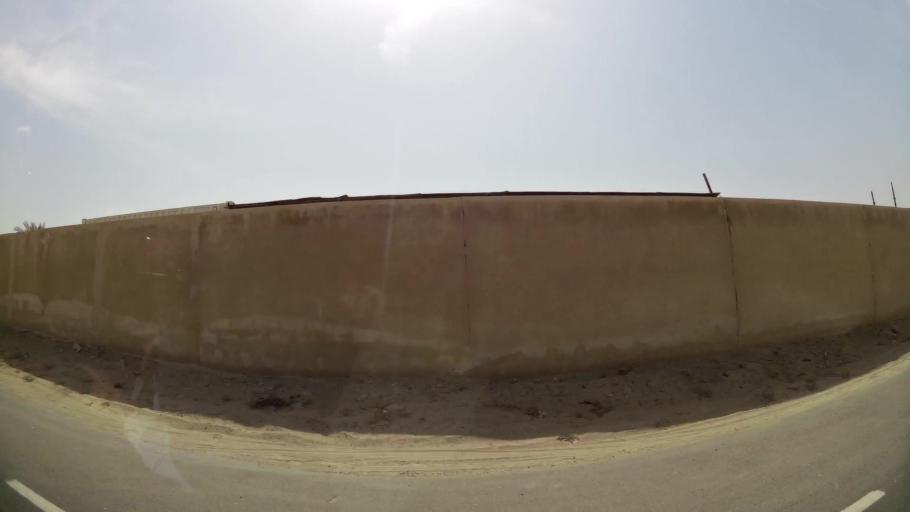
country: AE
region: Ash Shariqah
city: Sharjah
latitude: 25.2349
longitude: 55.4409
